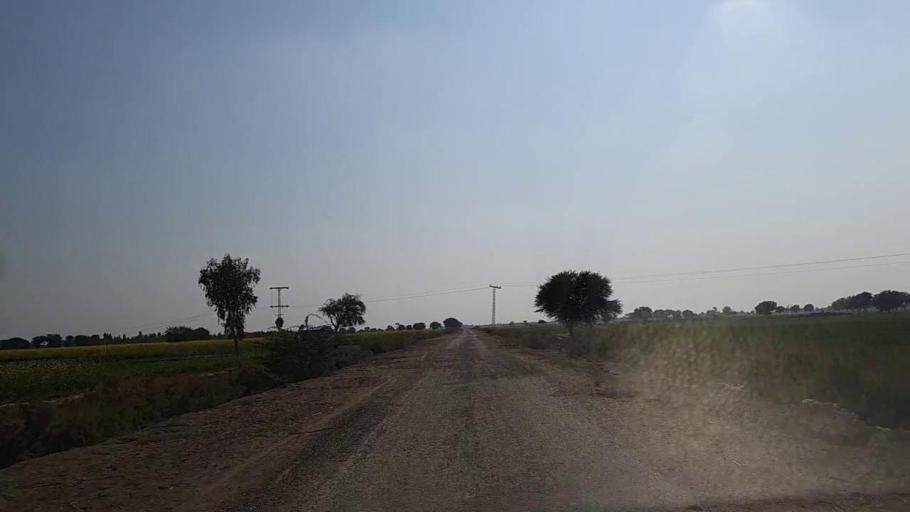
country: PK
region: Sindh
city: Jam Sahib
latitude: 26.2631
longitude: 68.5671
